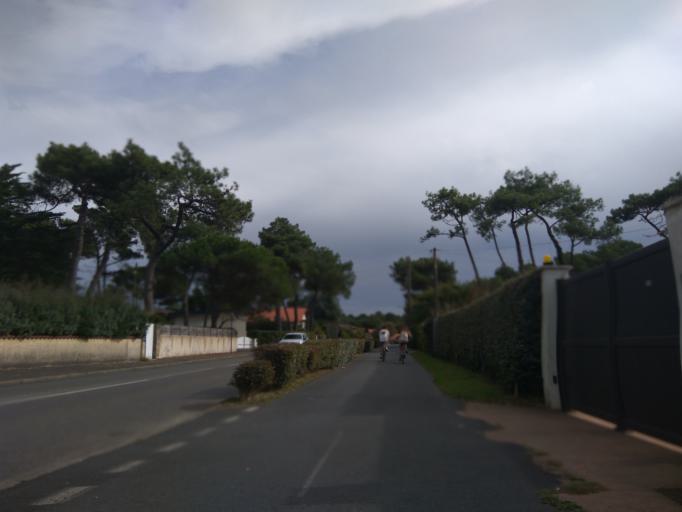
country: FR
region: Aquitaine
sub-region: Departement des Landes
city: Capbreton
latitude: 43.6410
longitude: -1.4413
